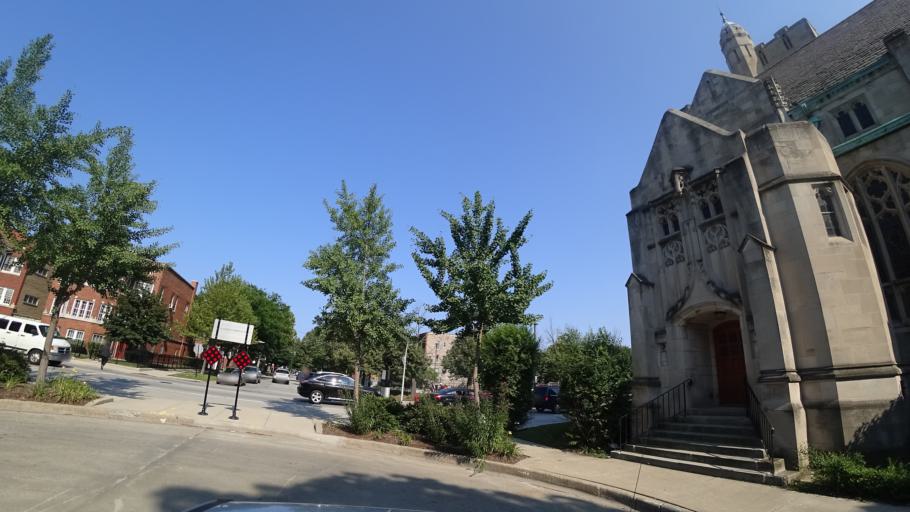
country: US
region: Illinois
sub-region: Cook County
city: Chicago
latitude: 41.7680
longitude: -87.5766
